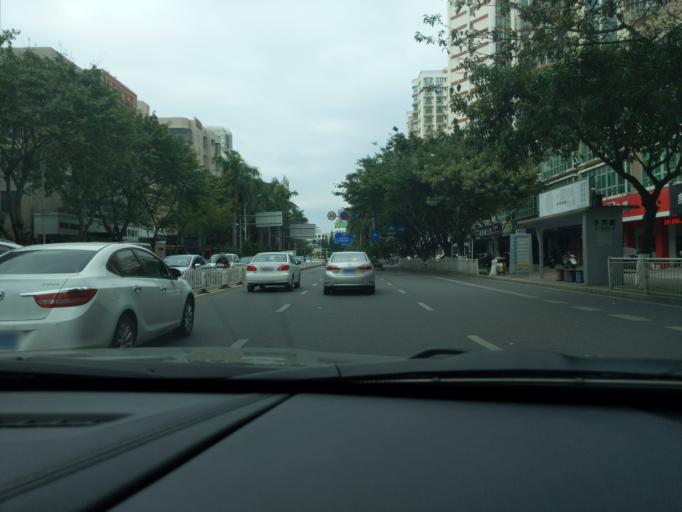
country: CN
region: Fujian
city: Shishi
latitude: 24.7456
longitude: 118.6357
